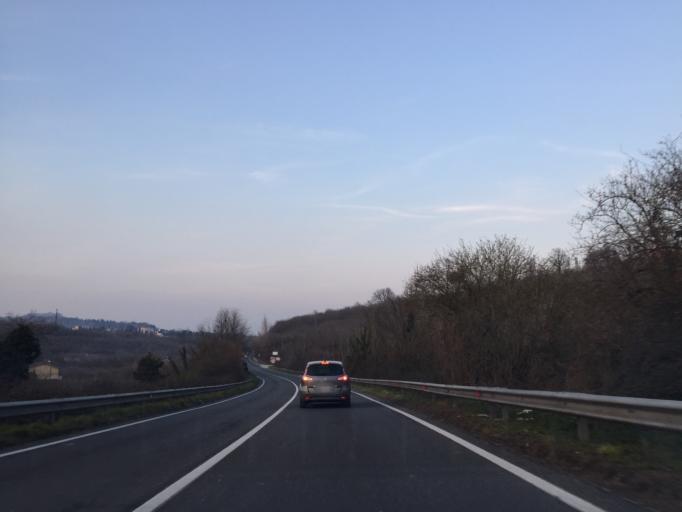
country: IT
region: Campania
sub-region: Provincia di Avellino
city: Avellino
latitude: 40.9050
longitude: 14.8087
